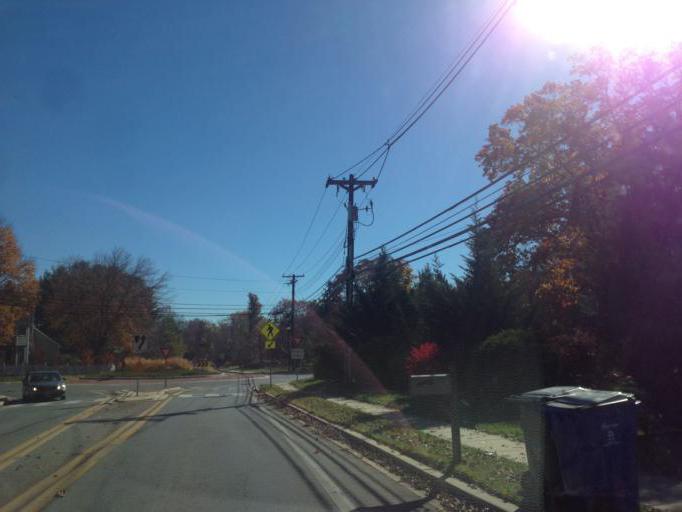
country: US
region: Maryland
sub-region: Howard County
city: Riverside
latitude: 39.2002
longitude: -76.8699
